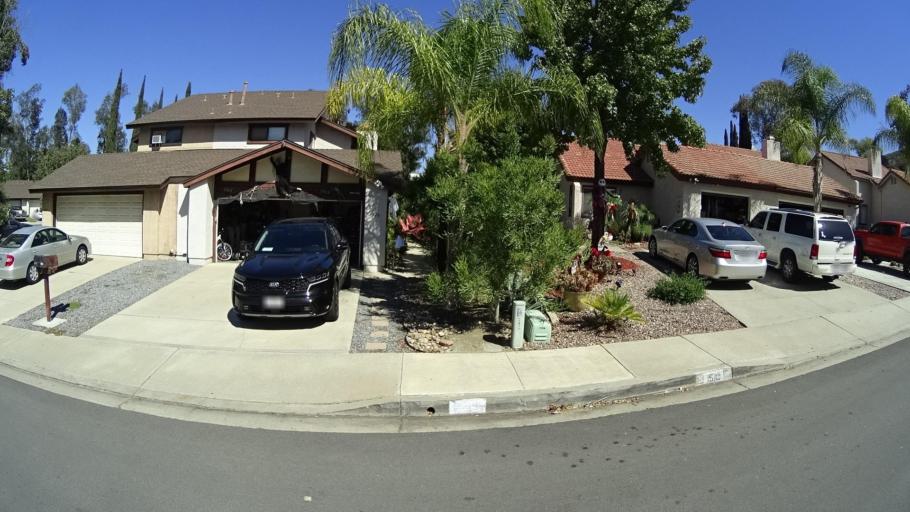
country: US
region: California
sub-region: San Diego County
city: Rancho San Diego
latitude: 32.7521
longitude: -116.9257
